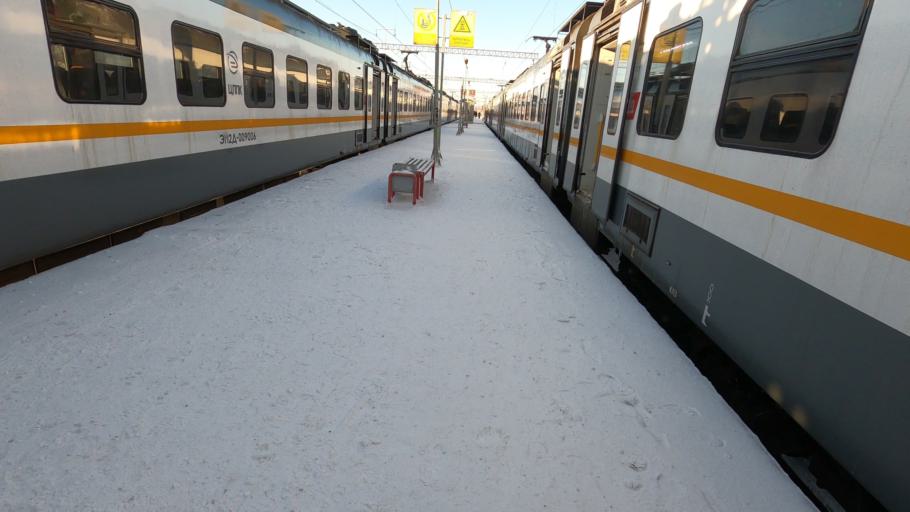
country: RU
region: Moskovskaya
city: Taldom
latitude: 56.7216
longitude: 37.5277
